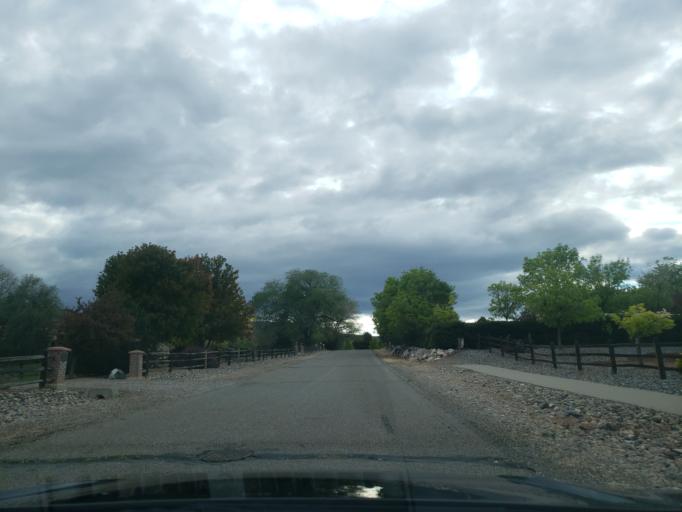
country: US
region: Colorado
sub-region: Mesa County
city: Redlands
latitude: 39.1064
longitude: -108.6766
